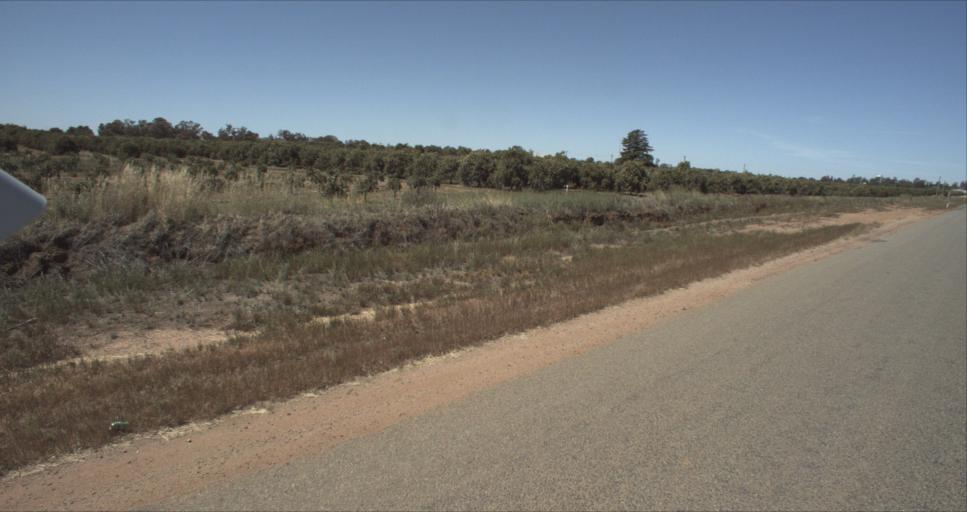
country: AU
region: New South Wales
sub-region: Leeton
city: Leeton
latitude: -34.5403
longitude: 146.3623
